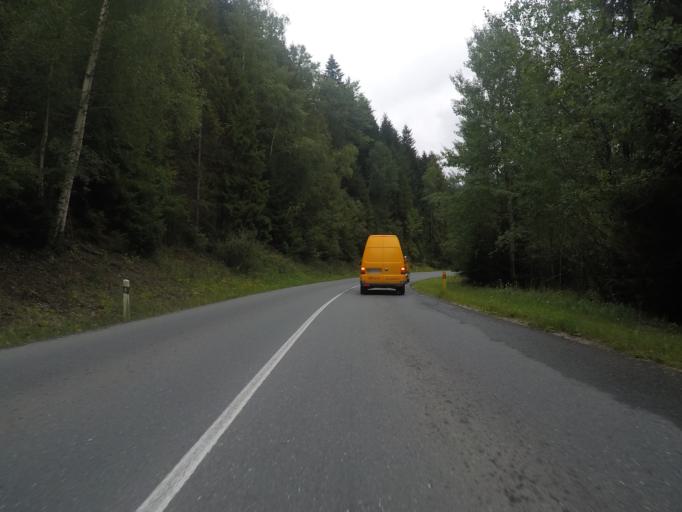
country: SK
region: Kosicky
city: Spisska Nova Ves
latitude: 48.8936
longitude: 20.5207
